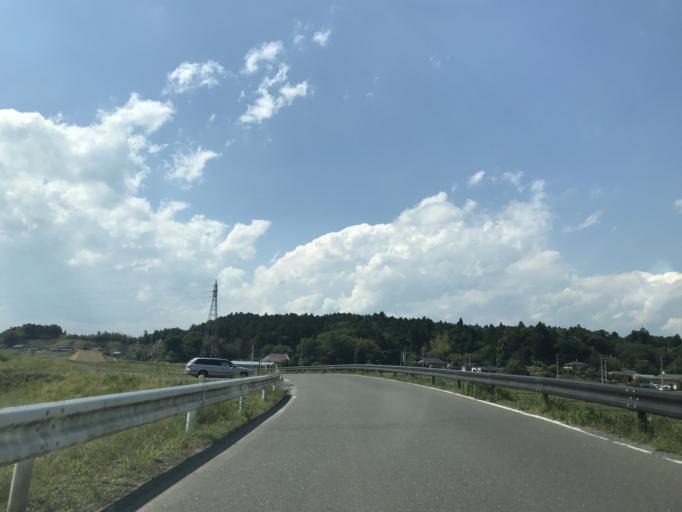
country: JP
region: Miyagi
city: Yamoto
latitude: 38.4182
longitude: 141.1430
